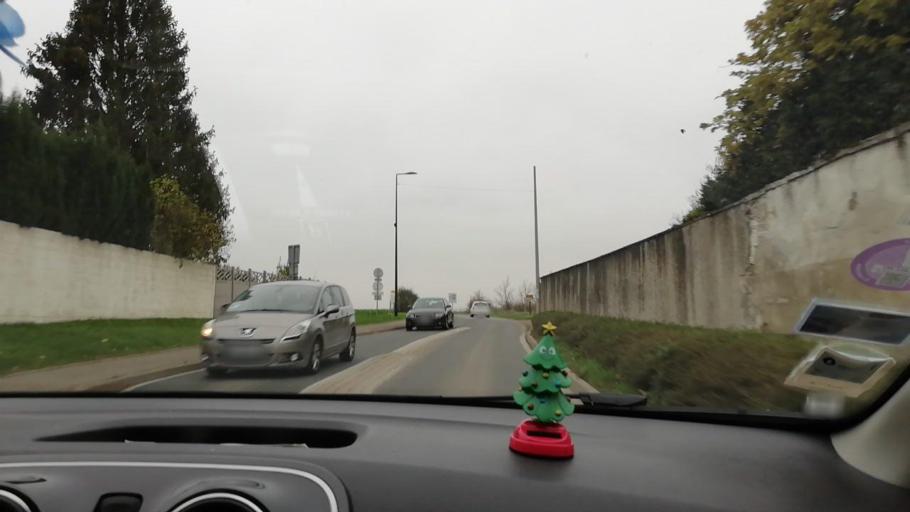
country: FR
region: Ile-de-France
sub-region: Departement de Seine-et-Marne
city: Claye-Souilly
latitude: 48.9655
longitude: 2.6957
